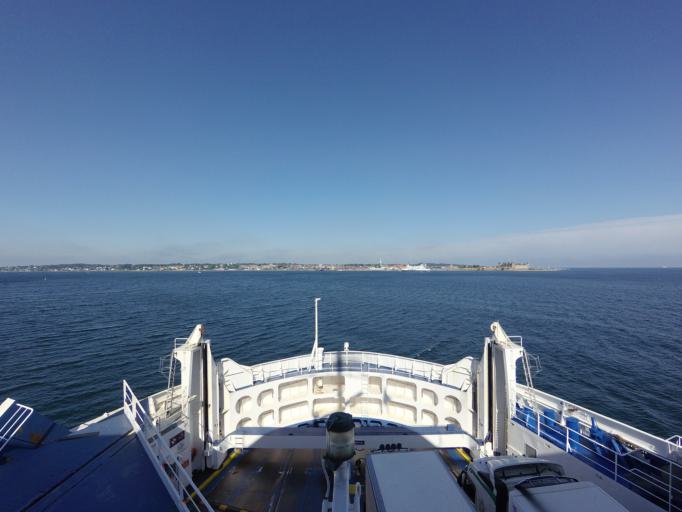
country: DK
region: Capital Region
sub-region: Helsingor Kommune
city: Helsingor
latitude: 56.0301
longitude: 12.6366
